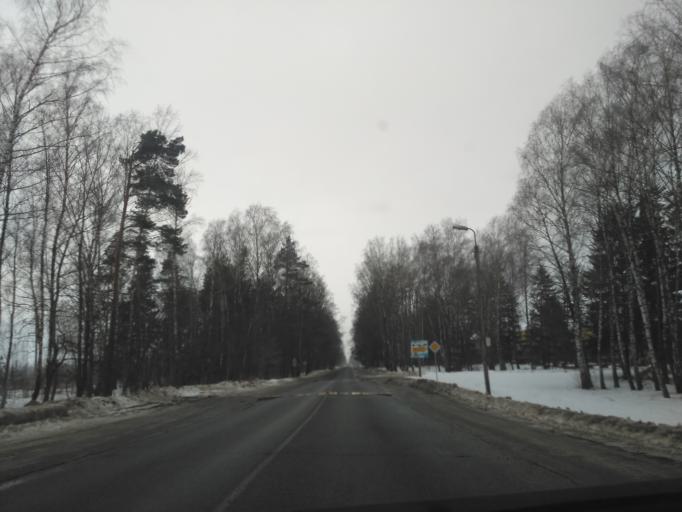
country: BY
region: Minsk
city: Horad Zhodzina
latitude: 54.0861
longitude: 28.3203
